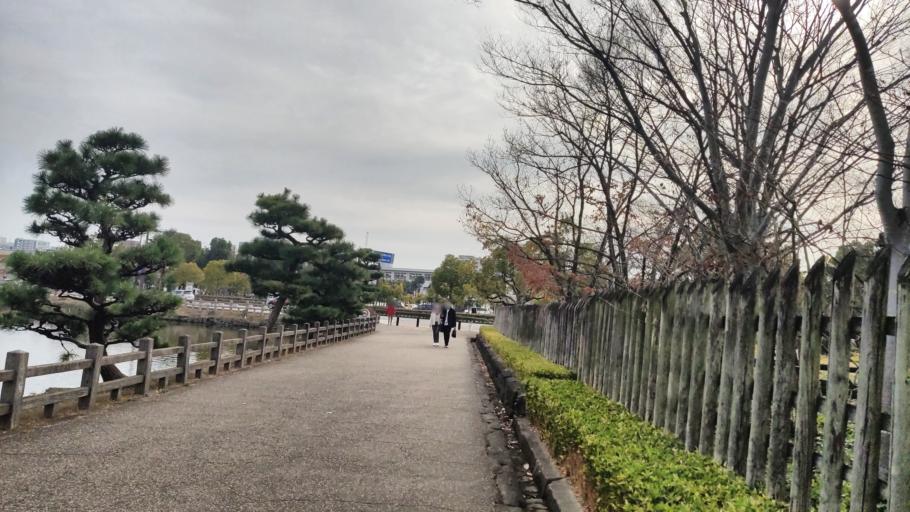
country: JP
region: Hyogo
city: Himeji
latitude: 34.8371
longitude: 134.6906
